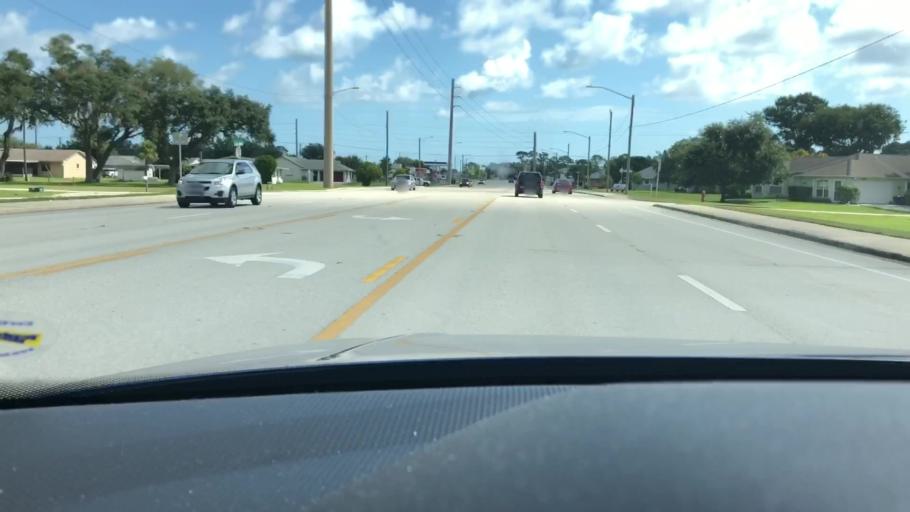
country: US
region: Florida
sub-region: Volusia County
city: Edgewater
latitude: 28.9684
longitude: -80.9058
